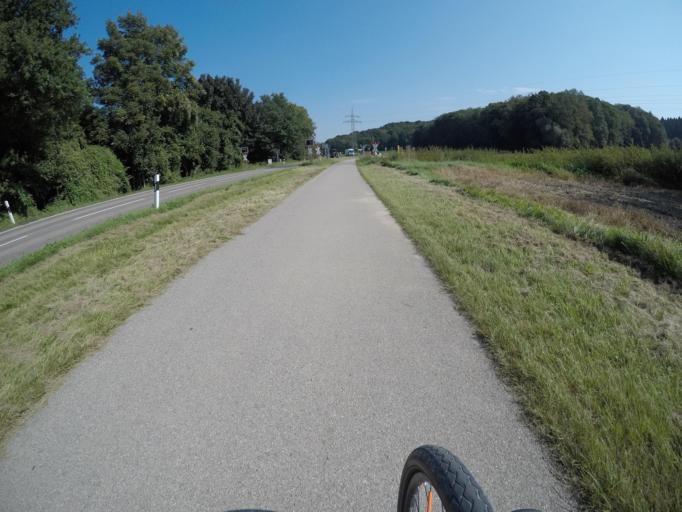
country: DE
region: Bavaria
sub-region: Swabia
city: Gundremmingen
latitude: 48.4884
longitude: 10.3857
